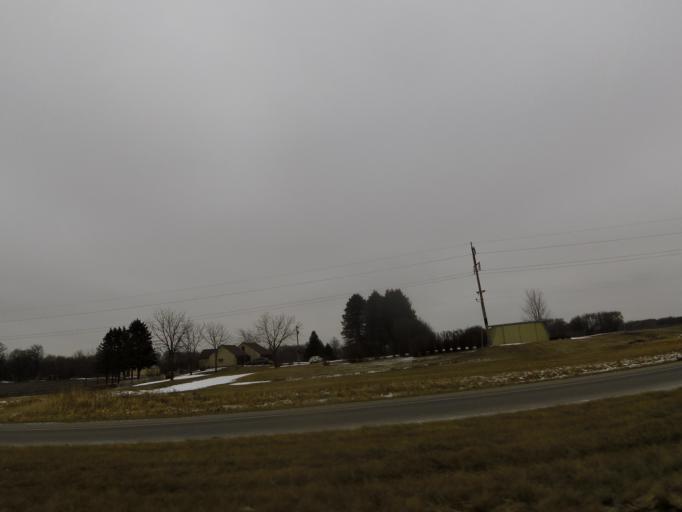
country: US
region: Minnesota
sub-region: Carver County
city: Waconia
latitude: 44.8297
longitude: -93.8225
